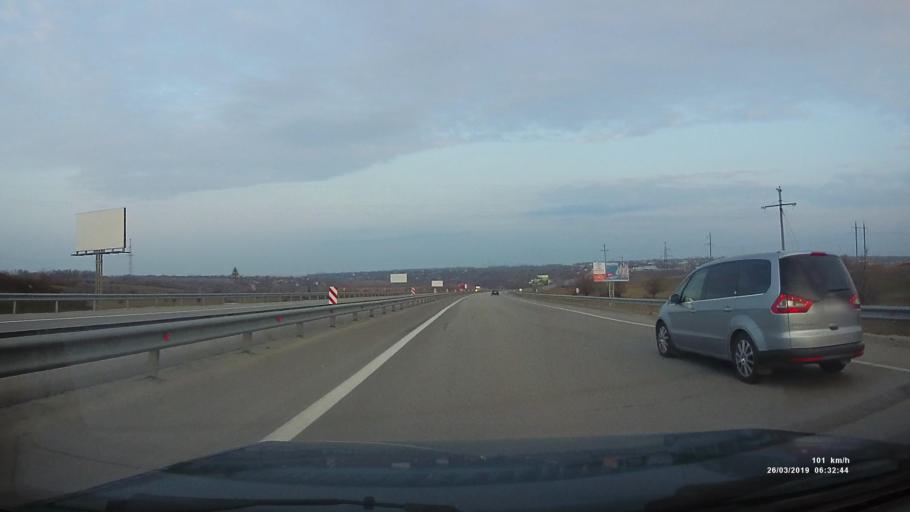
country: RU
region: Rostov
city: Kalinin
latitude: 47.2697
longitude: 39.5039
